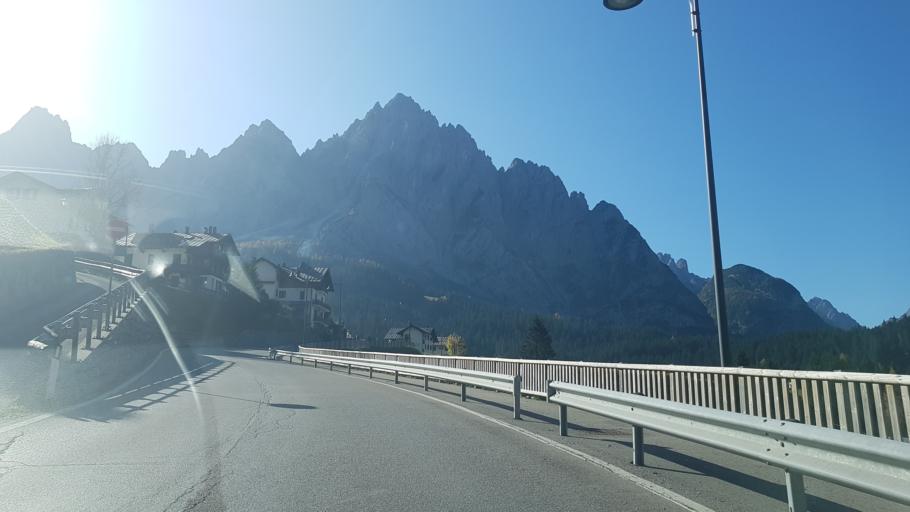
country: IT
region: Veneto
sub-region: Provincia di Belluno
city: Granvilla
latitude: 46.5718
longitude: 12.7218
